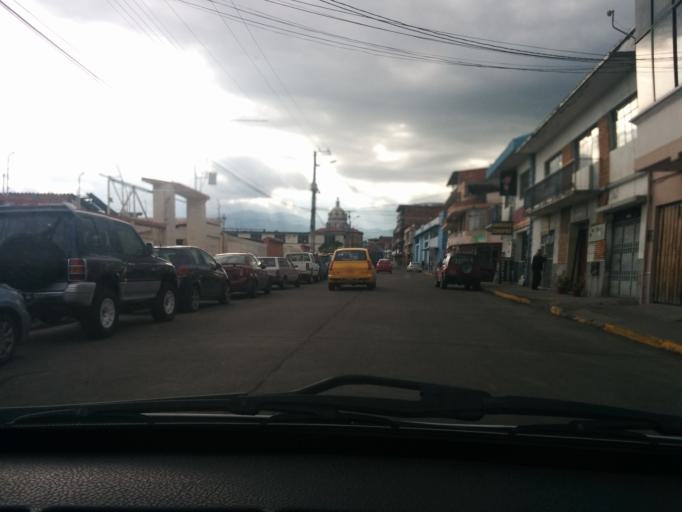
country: EC
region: Azuay
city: Cuenca
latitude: -2.8990
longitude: -78.9949
